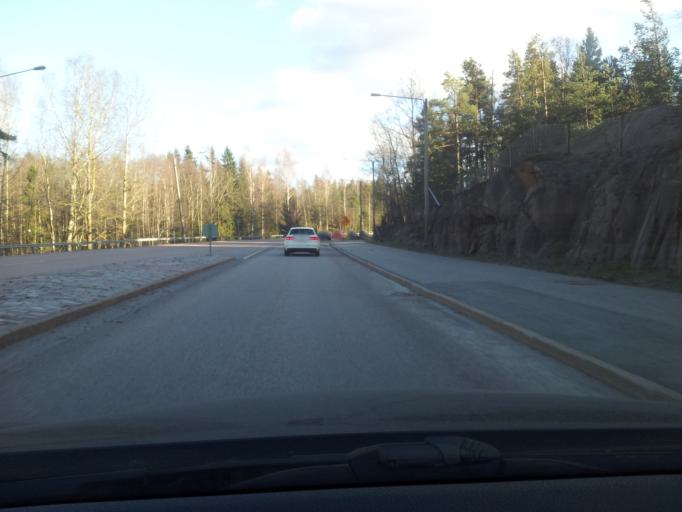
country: FI
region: Uusimaa
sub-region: Helsinki
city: Espoo
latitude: 60.1430
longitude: 24.6760
